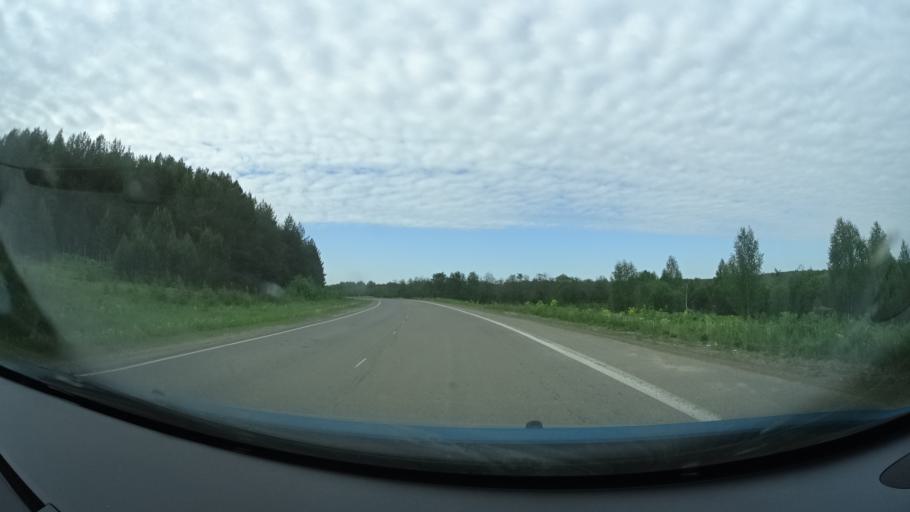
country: RU
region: Perm
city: Kuyeda
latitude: 56.5227
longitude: 55.6265
